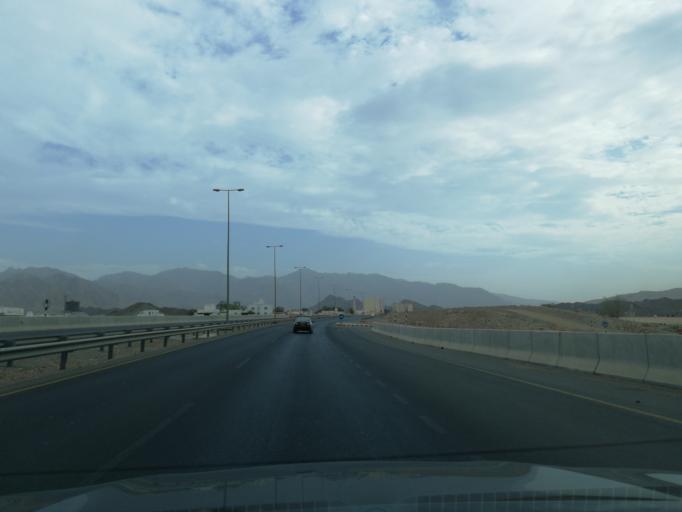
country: OM
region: Muhafazat Masqat
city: Bawshar
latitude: 23.5121
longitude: 58.3426
